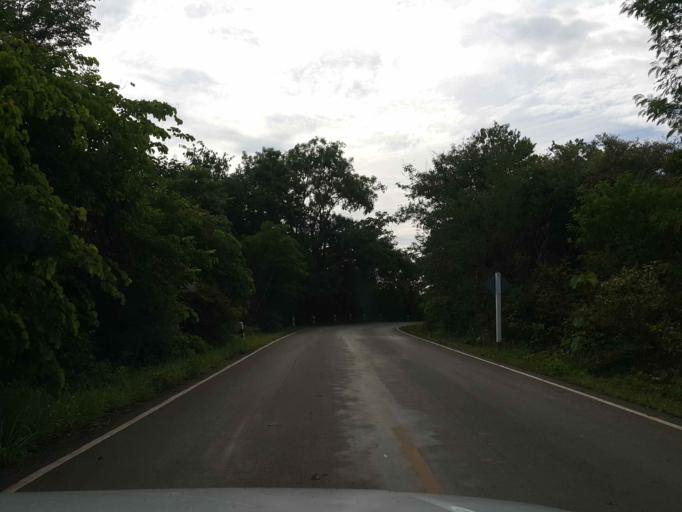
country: TH
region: Sukhothai
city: Thung Saliam
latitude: 17.3125
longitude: 99.5225
